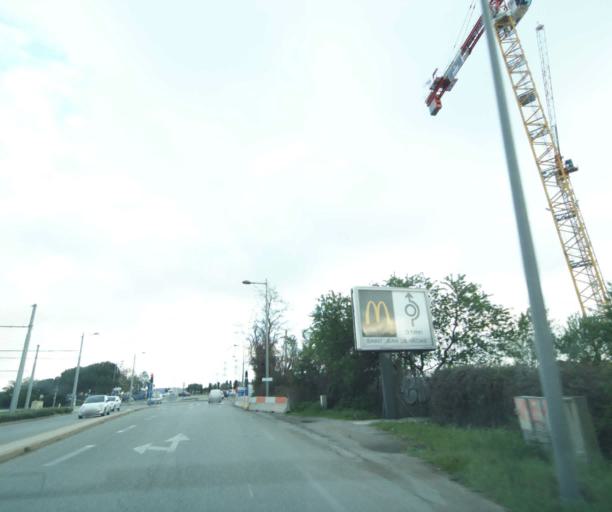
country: FR
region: Languedoc-Roussillon
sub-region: Departement de l'Herault
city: Saint-Jean-de-Vedas
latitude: 43.5712
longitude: 3.8364
